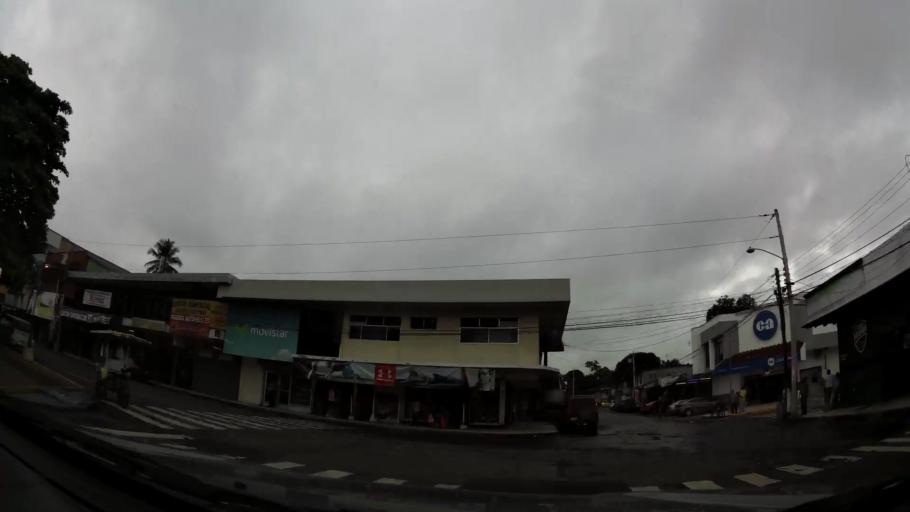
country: PA
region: Chiriqui
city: La Concepcion
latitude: 8.5179
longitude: -82.6195
